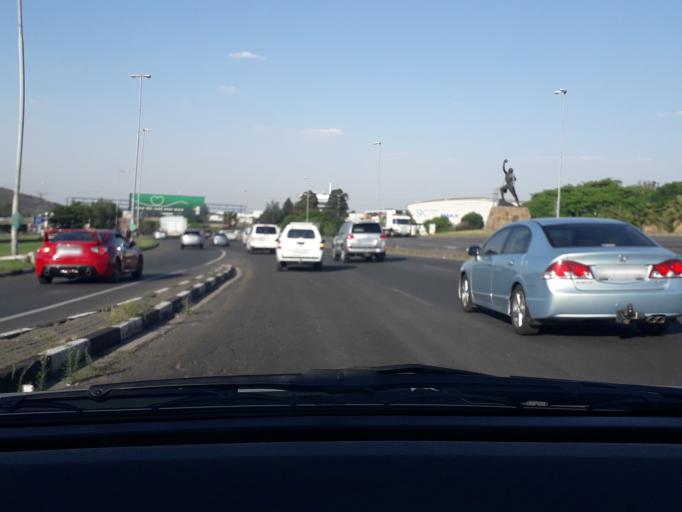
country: ZA
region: Gauteng
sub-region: City of Johannesburg Metropolitan Municipality
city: Johannesburg
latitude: -26.1819
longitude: 28.1115
